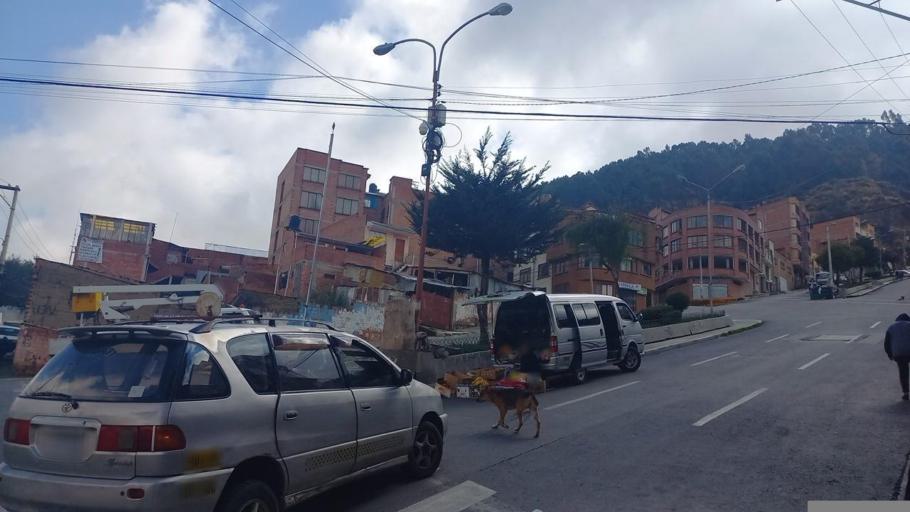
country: BO
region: La Paz
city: La Paz
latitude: -16.4675
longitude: -68.1507
